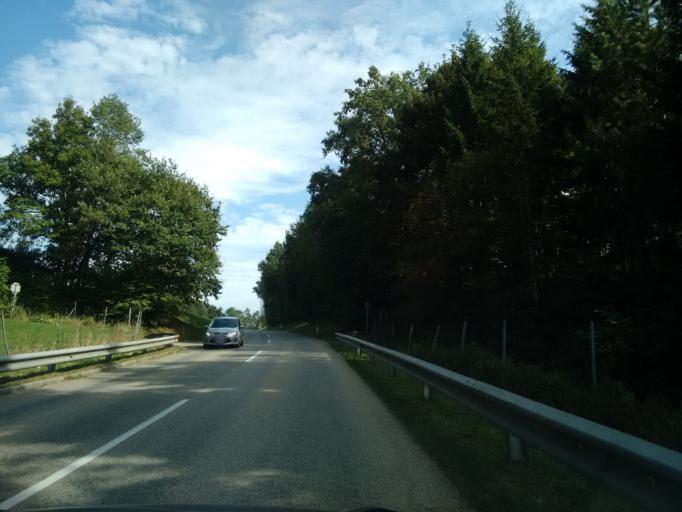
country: AT
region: Upper Austria
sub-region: Wels-Land
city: Thalheim bei Wels
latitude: 48.1295
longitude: 14.0754
